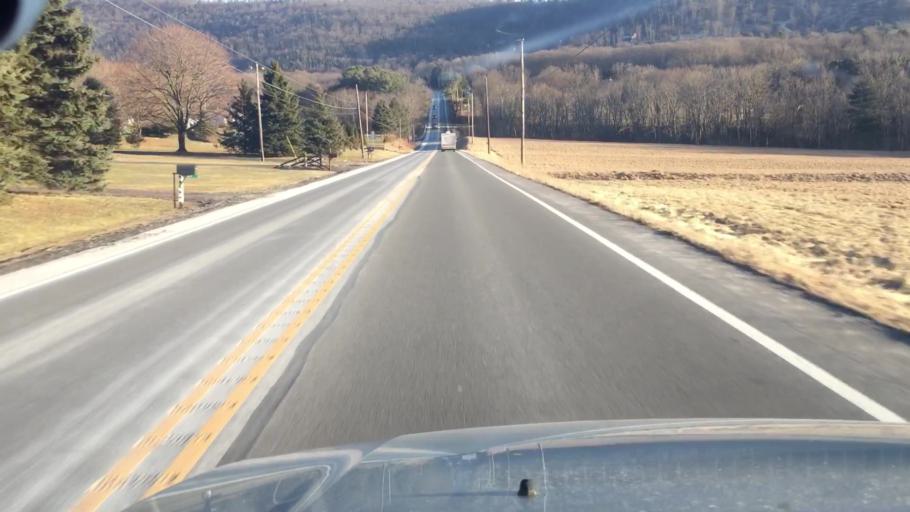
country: US
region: Pennsylvania
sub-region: Luzerne County
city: Nescopeck
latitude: 41.0389
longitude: -76.1379
